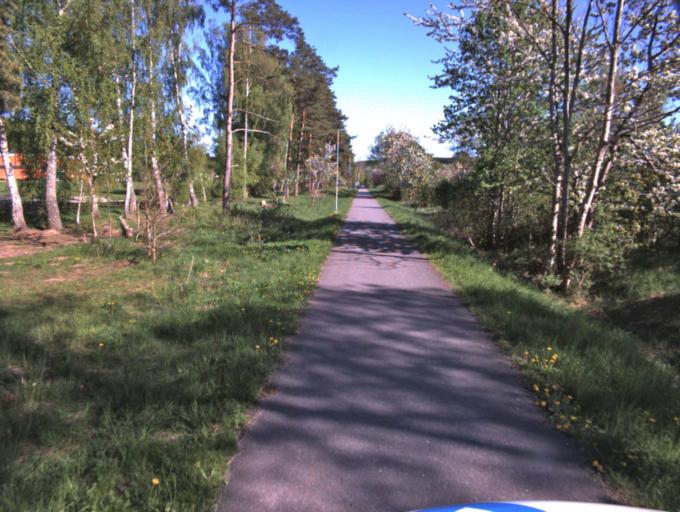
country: SE
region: Skane
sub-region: Kristianstads Kommun
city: Degeberga
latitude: 55.8305
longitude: 14.0860
